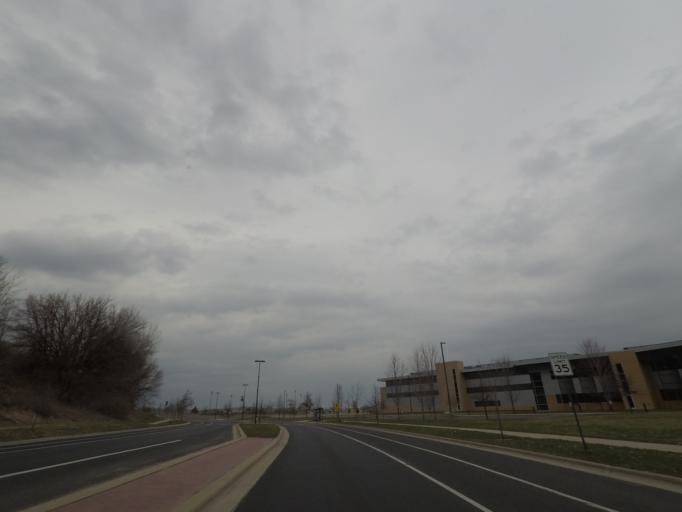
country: US
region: Wisconsin
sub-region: Dane County
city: Middleton
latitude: 43.1067
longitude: -89.5360
